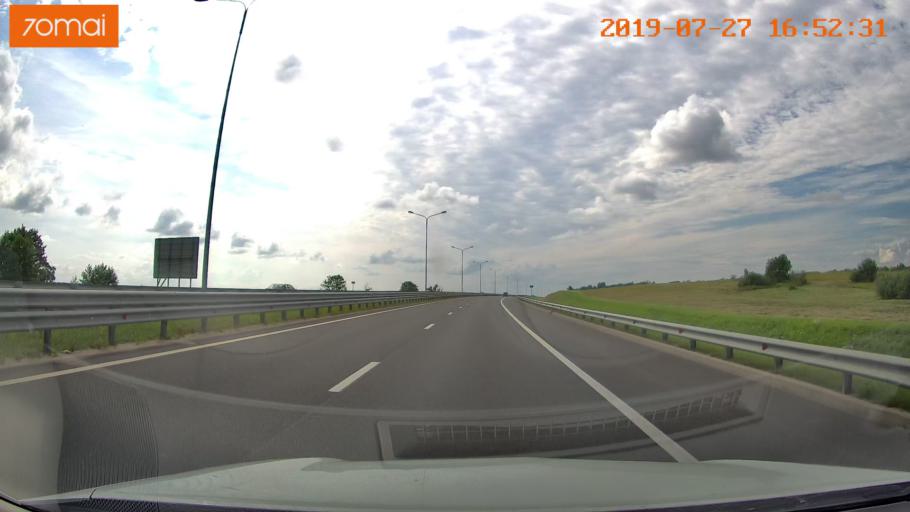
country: RU
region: Kaliningrad
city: Gvardeysk
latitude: 54.6837
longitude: 20.8565
